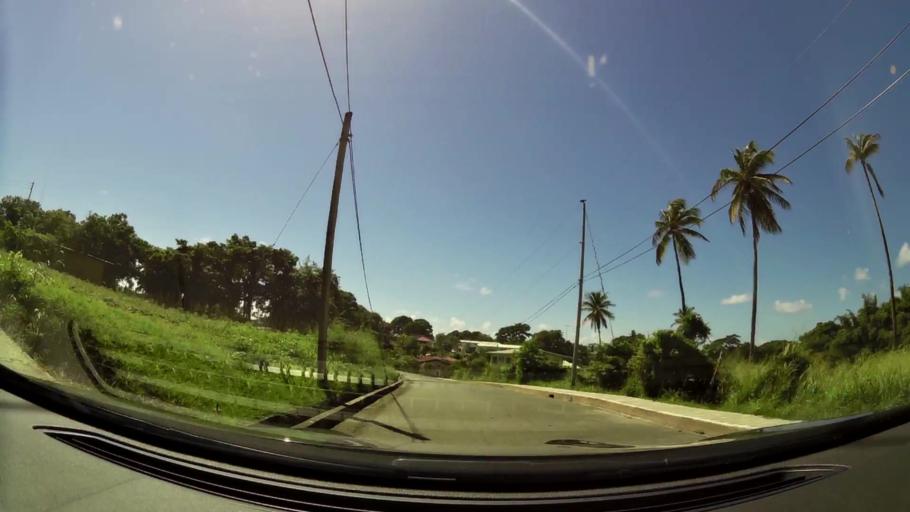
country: TT
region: Tobago
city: Scarborough
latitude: 11.1765
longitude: -60.7794
